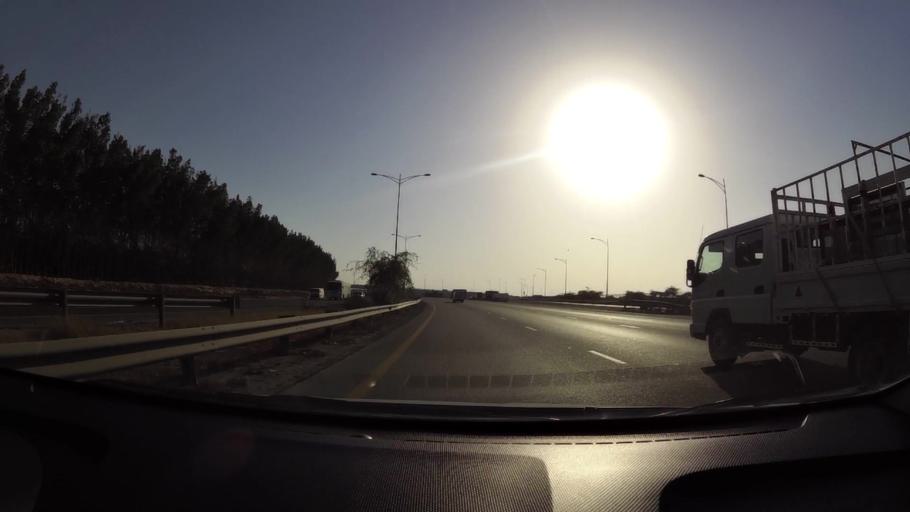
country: AE
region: Ajman
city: Ajman
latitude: 25.3591
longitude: 55.4863
